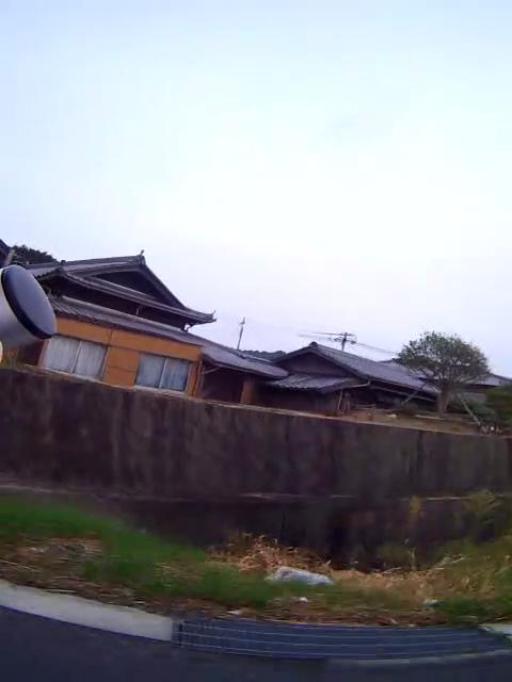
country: JP
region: Hyogo
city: Fukura
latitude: 34.3033
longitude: 134.8051
